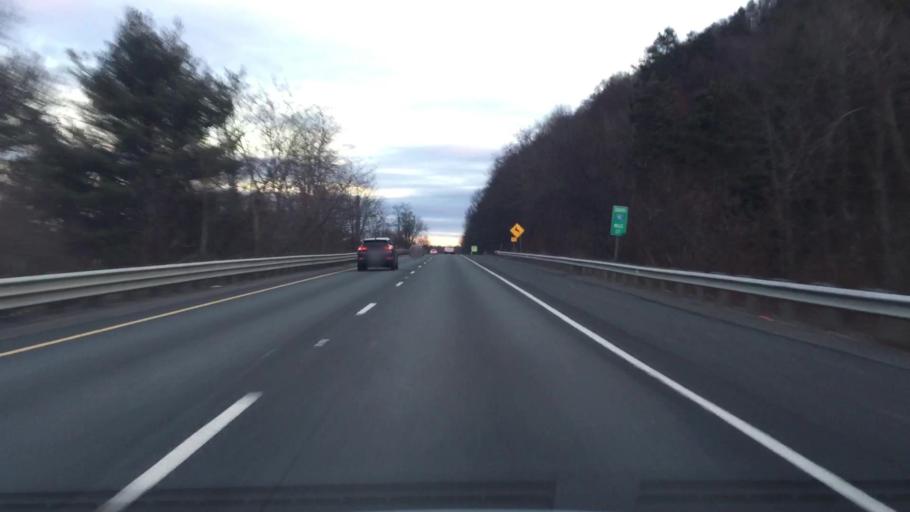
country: US
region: Massachusetts
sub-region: Hampshire County
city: Northampton
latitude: 42.2857
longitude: -72.6191
